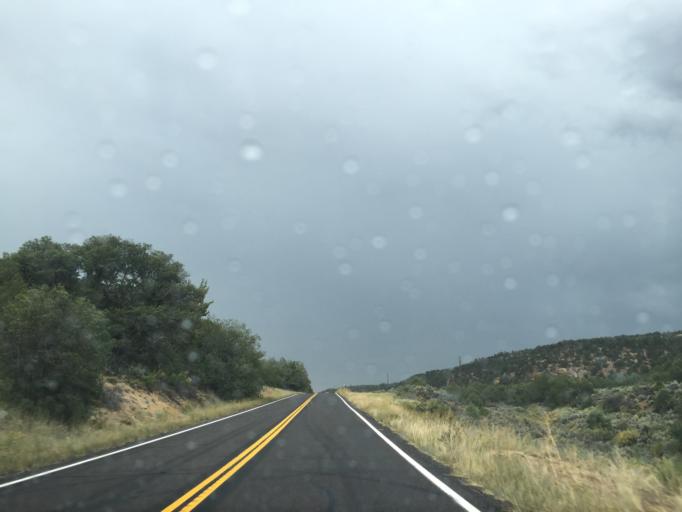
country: US
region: Utah
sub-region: Washington County
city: Hildale
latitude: 37.2379
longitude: -112.8481
